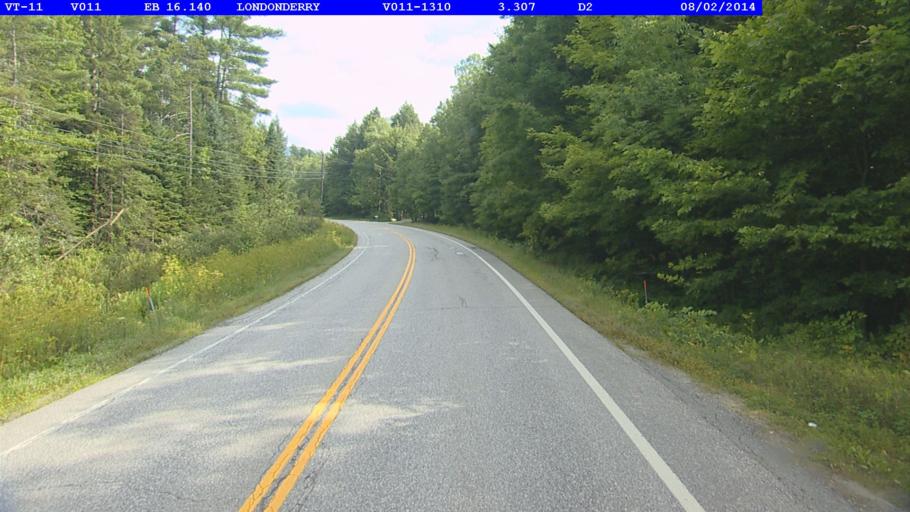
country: US
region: Vermont
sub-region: Windsor County
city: Chester
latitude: 43.2199
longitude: -72.7926
